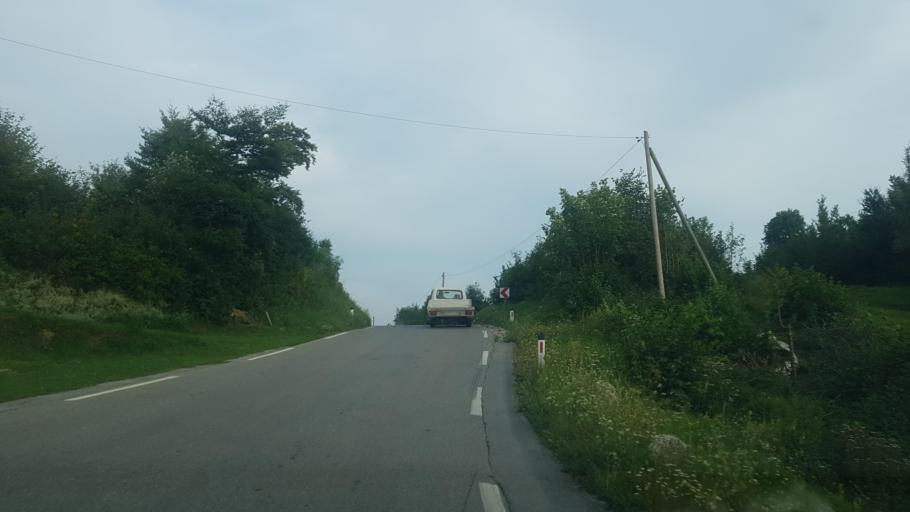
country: SI
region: Vipava
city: Vipava
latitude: 45.8591
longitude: 14.0701
